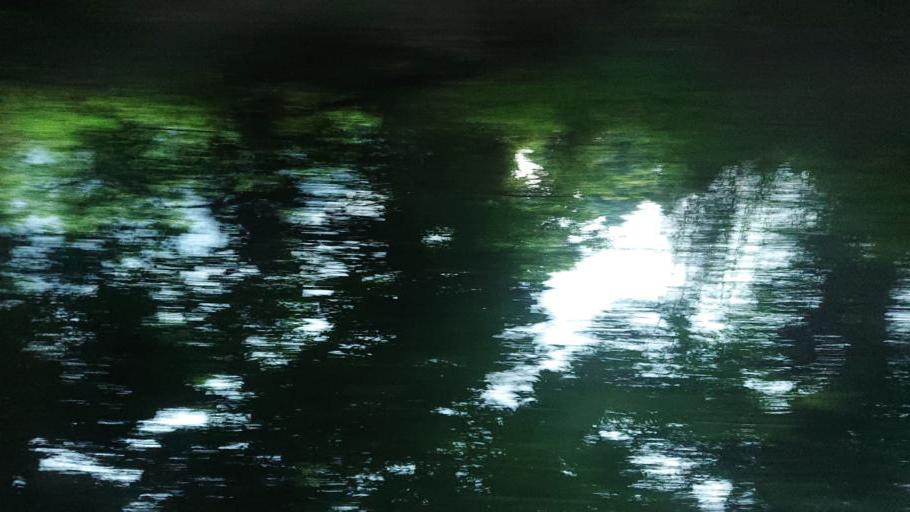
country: TW
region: Taiwan
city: Lugu
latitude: 23.5916
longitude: 120.7238
